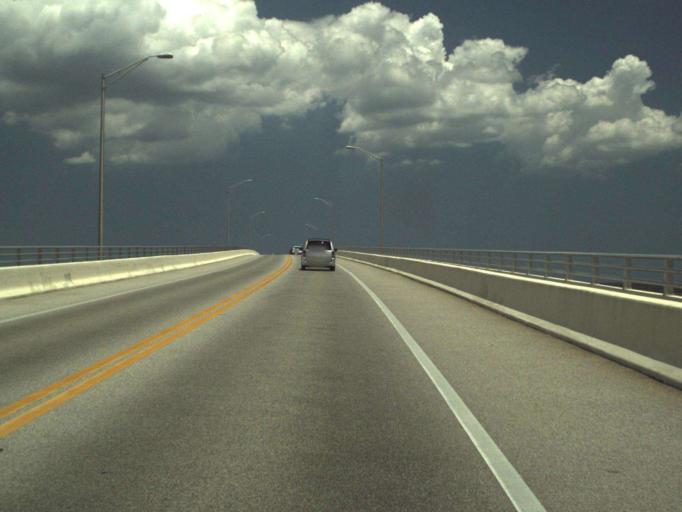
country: US
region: Florida
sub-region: Brevard County
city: Titusville
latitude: 28.6193
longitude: -80.8000
